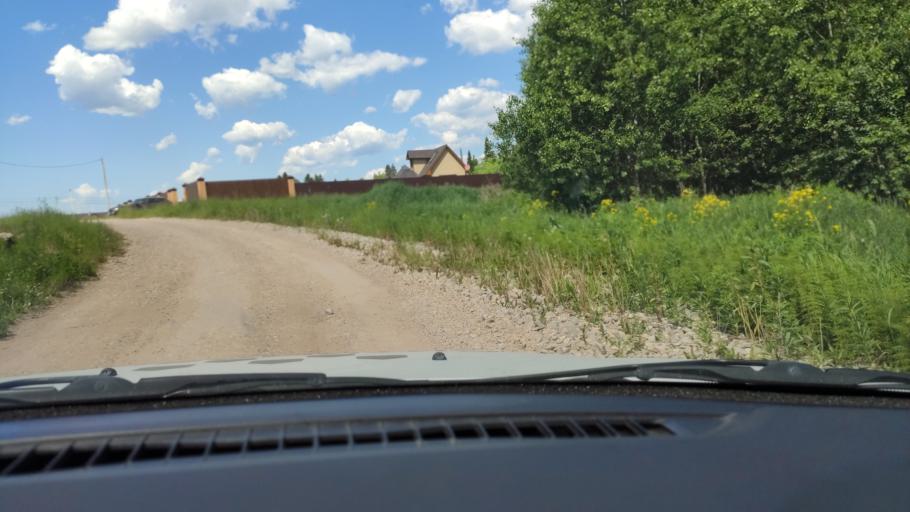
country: RU
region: Perm
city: Ferma
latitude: 57.9433
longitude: 56.3429
